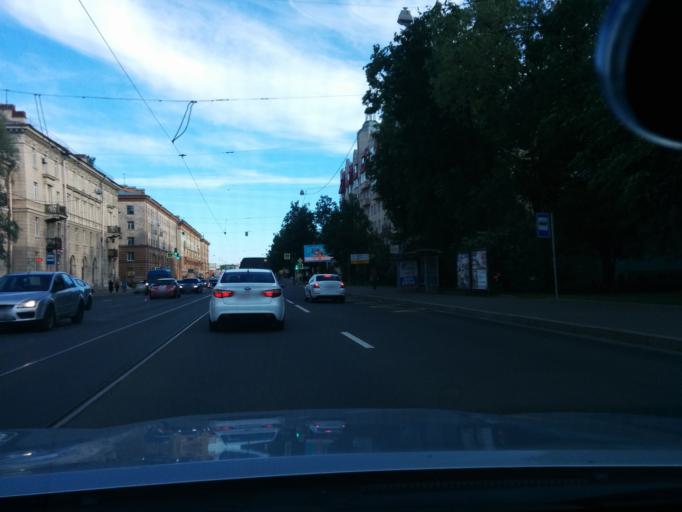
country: RU
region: Leningrad
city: Udel'naya
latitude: 60.0139
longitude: 30.3234
